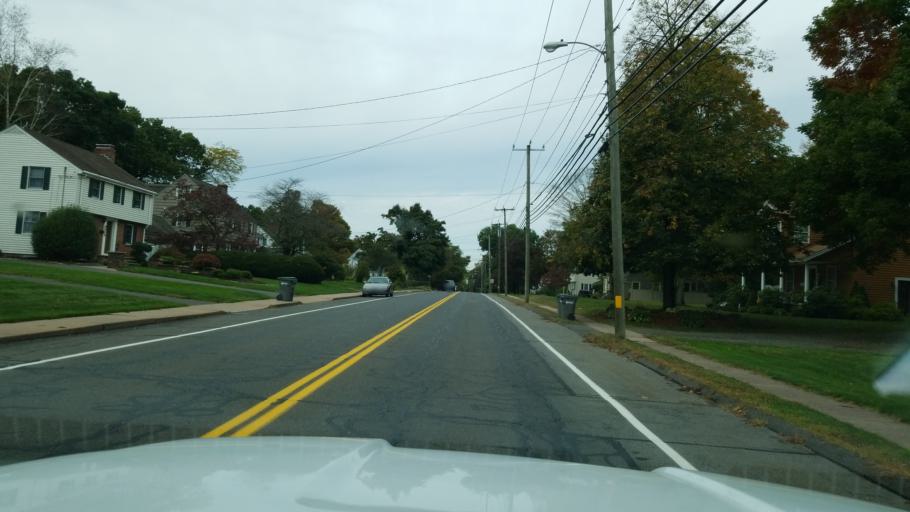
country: US
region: Connecticut
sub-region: Hartford County
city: Manchester
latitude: 41.7739
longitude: -72.4988
